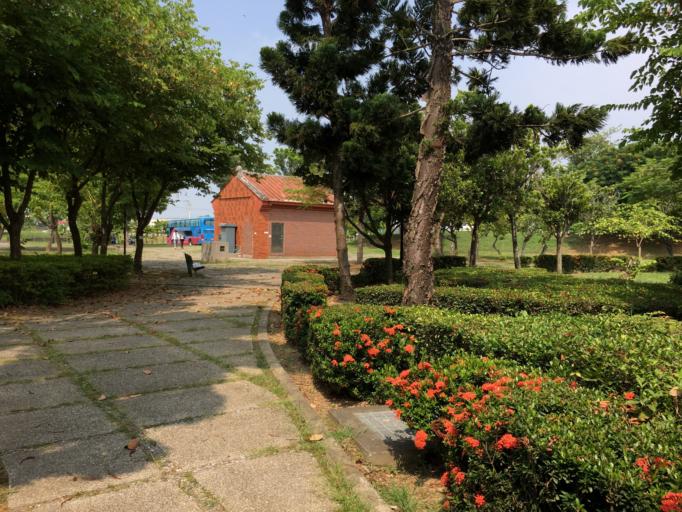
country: TW
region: Taiwan
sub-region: Chiayi
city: Jiayi Shi
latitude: 23.5446
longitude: 120.4321
